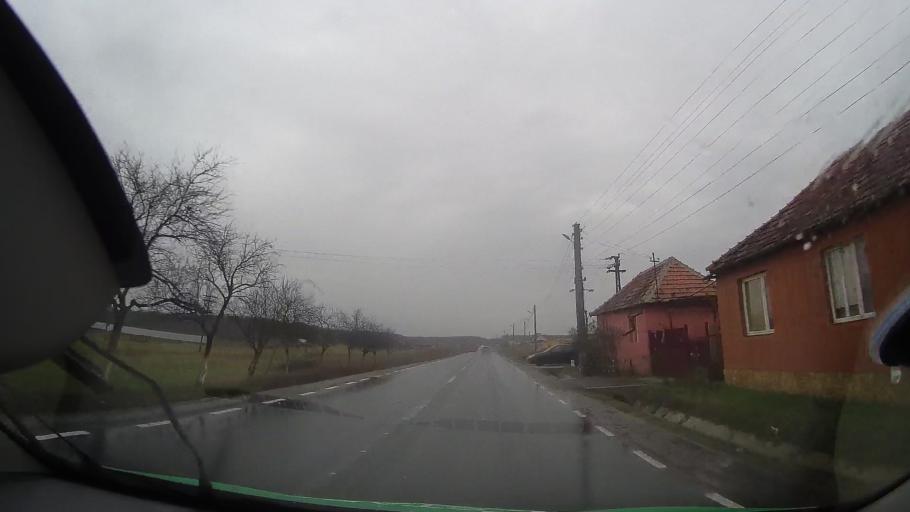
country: RO
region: Bihor
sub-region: Comuna Olcea
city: Olcea
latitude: 46.6856
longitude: 21.9661
